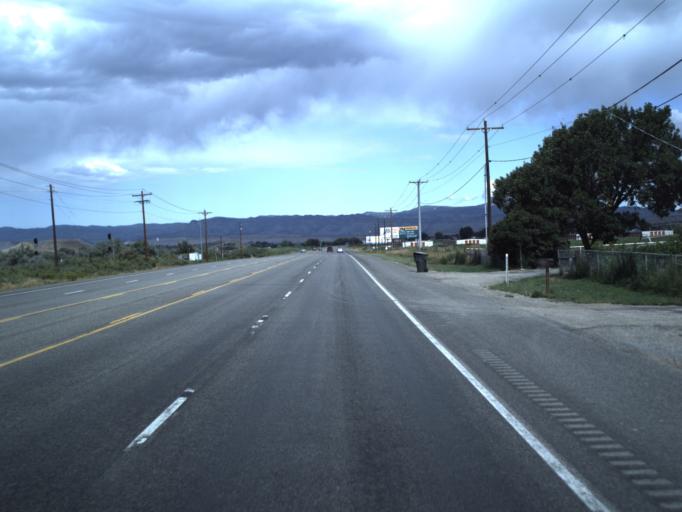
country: US
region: Utah
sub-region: Carbon County
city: Wellington
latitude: 39.5613
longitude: -110.7678
